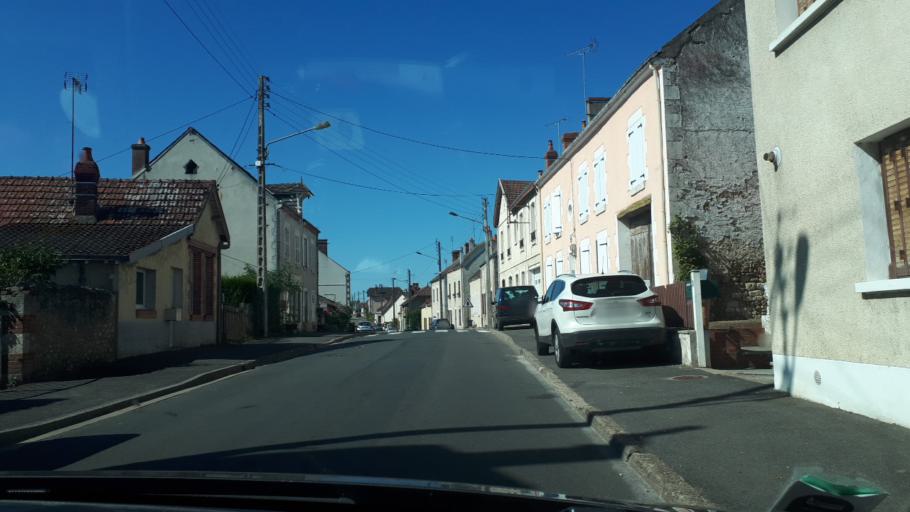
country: FR
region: Centre
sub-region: Departement du Loiret
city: Briare
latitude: 47.5891
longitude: 2.7438
